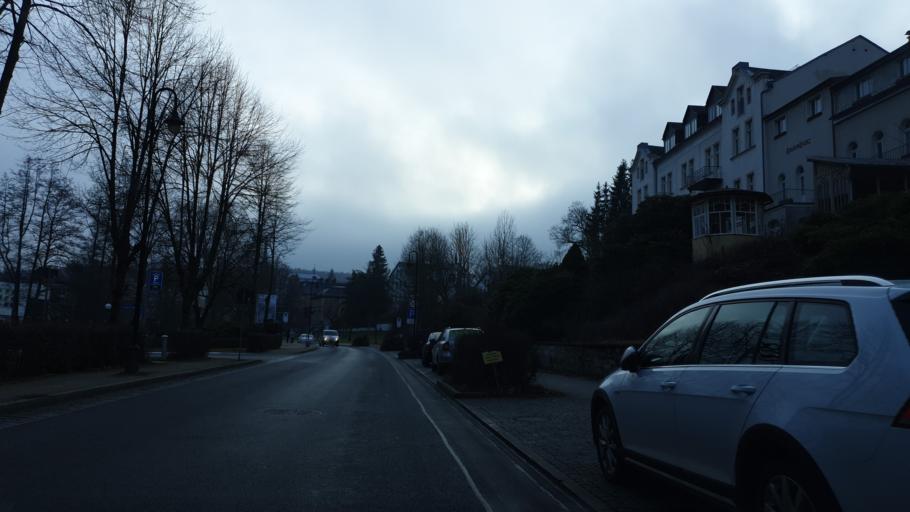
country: DE
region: Saxony
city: Bad Elster
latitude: 50.2857
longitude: 12.2387
